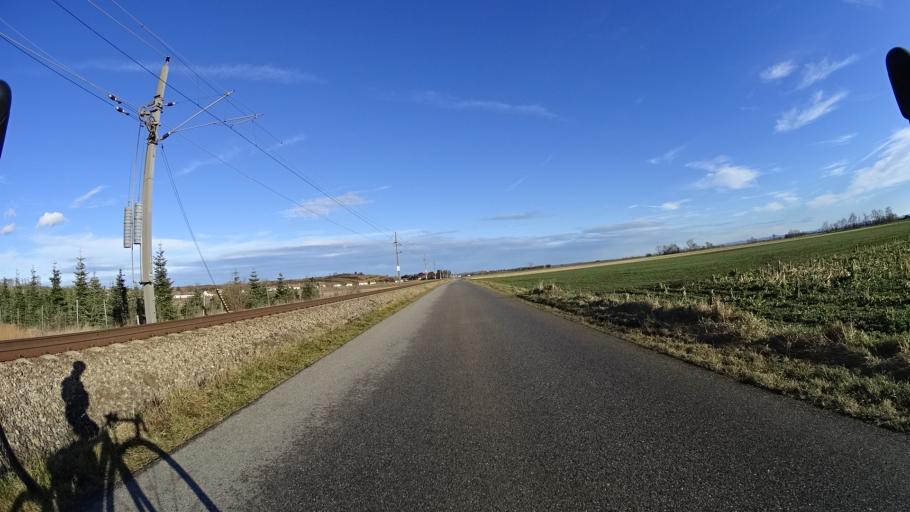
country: AT
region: Lower Austria
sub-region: Politischer Bezirk Tulln
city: Fels am Wagram
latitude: 48.4267
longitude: 15.8078
